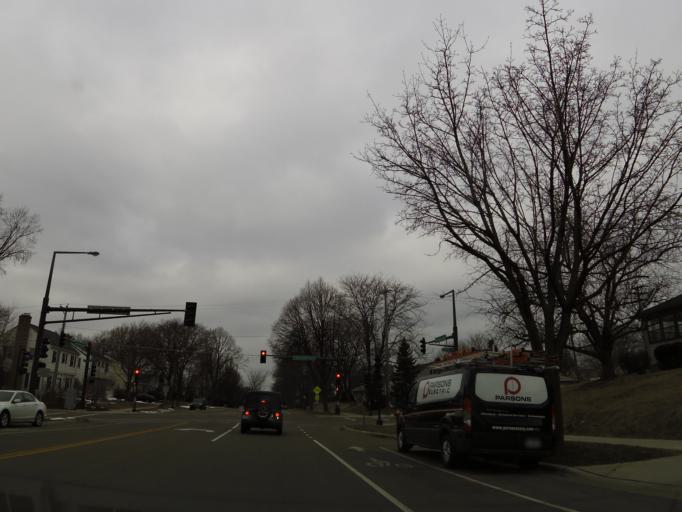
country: US
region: Minnesota
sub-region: Dakota County
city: Mendota Heights
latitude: 44.9126
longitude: -93.1767
